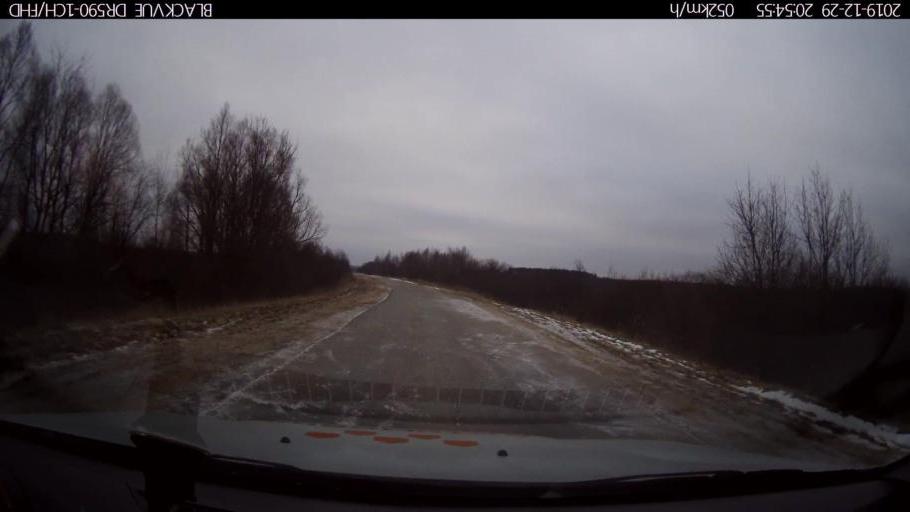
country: RU
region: Nizjnij Novgorod
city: Afonino
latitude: 56.1606
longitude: 43.9913
